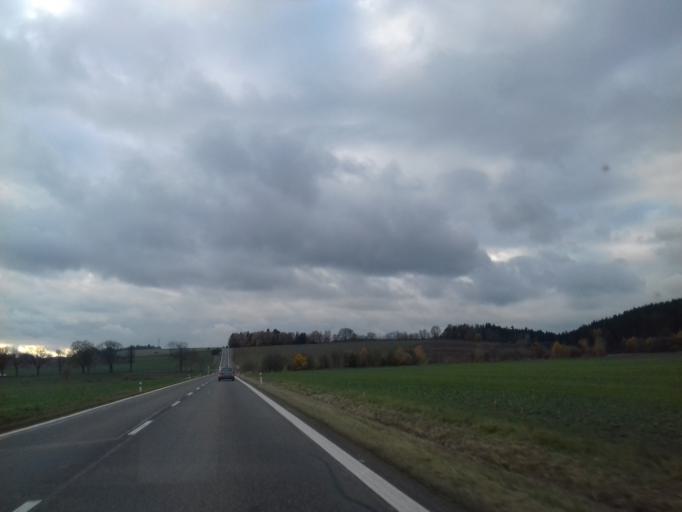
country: CZ
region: Pardubicky
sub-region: Okres Svitavy
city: Svitavy
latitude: 49.7515
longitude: 16.4346
